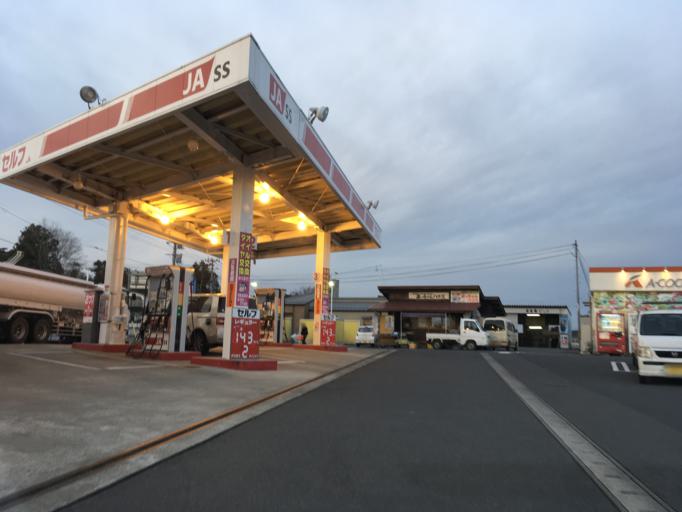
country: JP
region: Miyagi
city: Kogota
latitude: 38.6505
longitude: 141.0764
